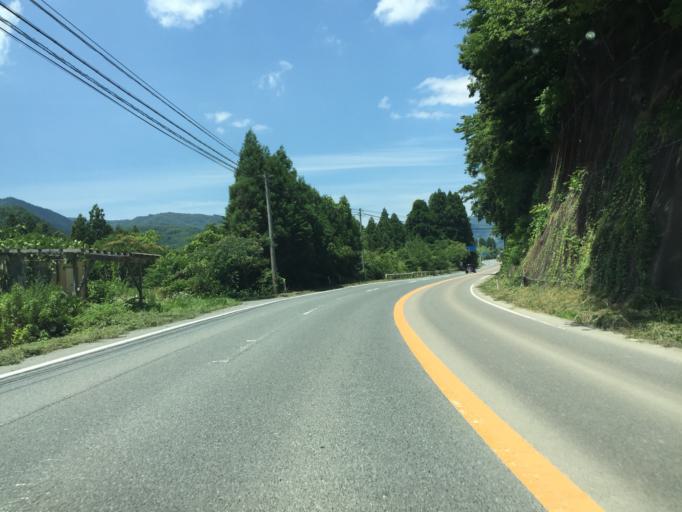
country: JP
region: Miyagi
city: Marumori
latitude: 37.7664
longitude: 140.8505
